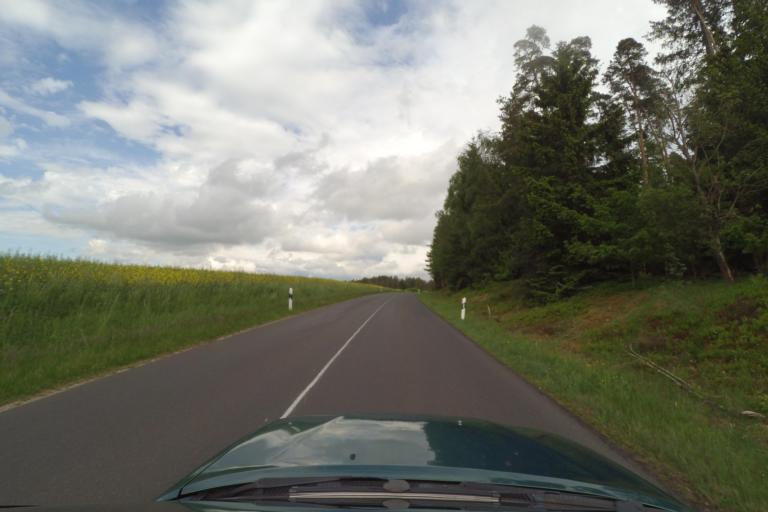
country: DE
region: Bavaria
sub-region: Upper Palatinate
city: Schwarzenbach
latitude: 49.8388
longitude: 12.3460
